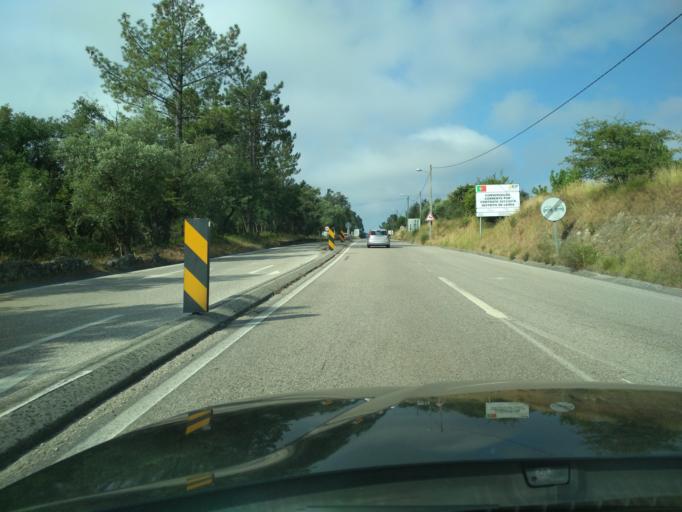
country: PT
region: Coimbra
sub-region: Soure
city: Soure
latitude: 40.0328
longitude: -8.5646
